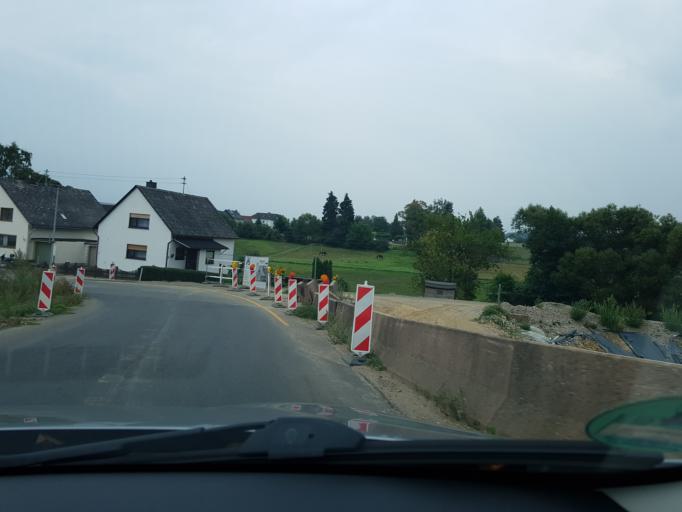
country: DE
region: Rheinland-Pfalz
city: Miehlen
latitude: 50.2291
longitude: 7.8249
